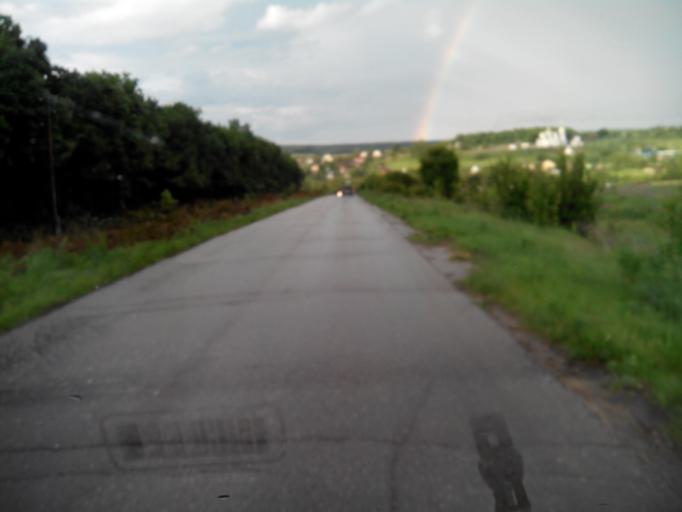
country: RU
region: Penza
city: Zasechnoye
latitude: 53.0678
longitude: 45.0108
